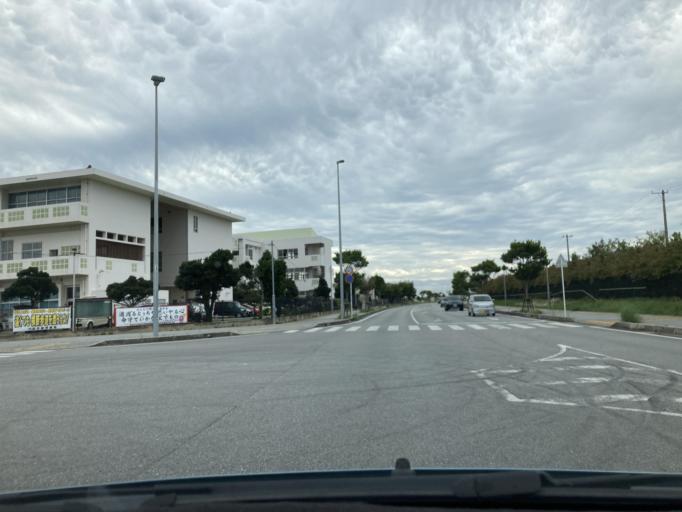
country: JP
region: Okinawa
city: Ishikawa
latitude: 26.3968
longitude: 127.7409
